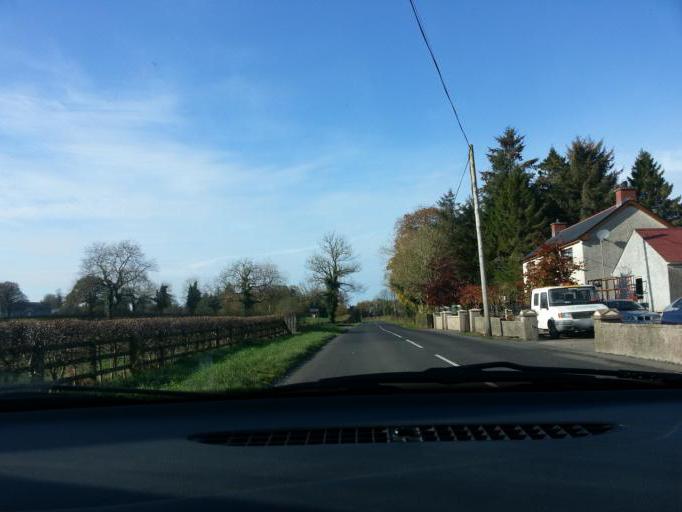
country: GB
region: Northern Ireland
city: Lisnaskea
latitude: 54.2248
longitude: -7.3431
